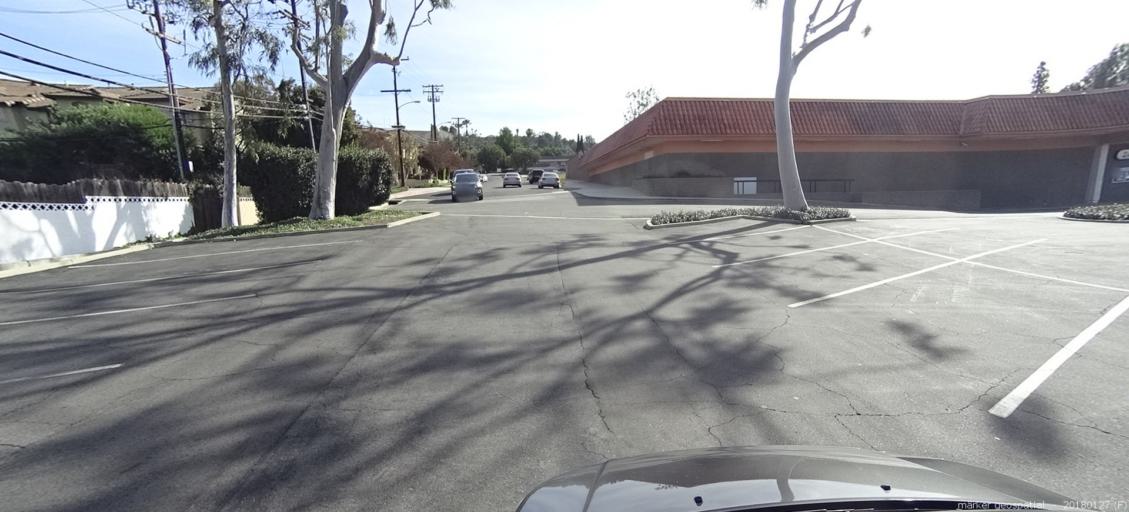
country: US
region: California
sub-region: Los Angeles County
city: Diamond Bar
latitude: 34.0213
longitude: -117.8087
